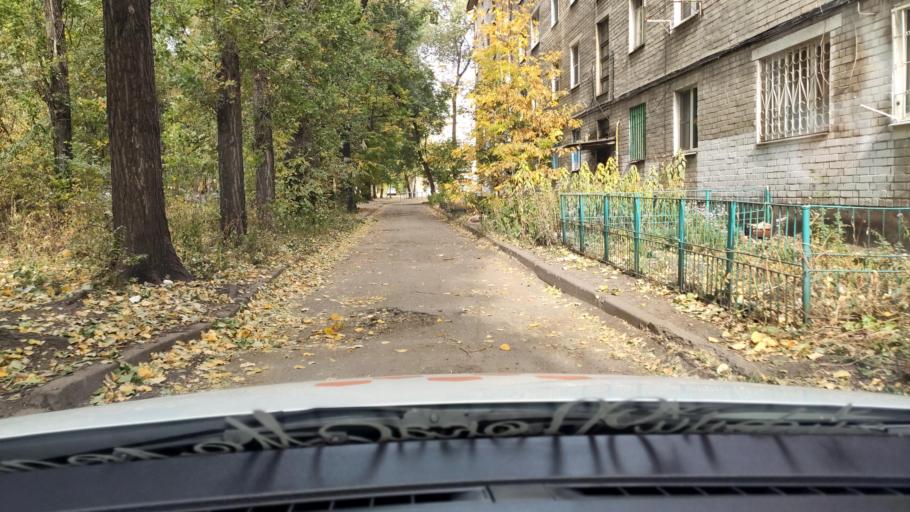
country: RU
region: Voronezj
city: Voronezh
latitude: 51.6810
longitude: 39.1926
